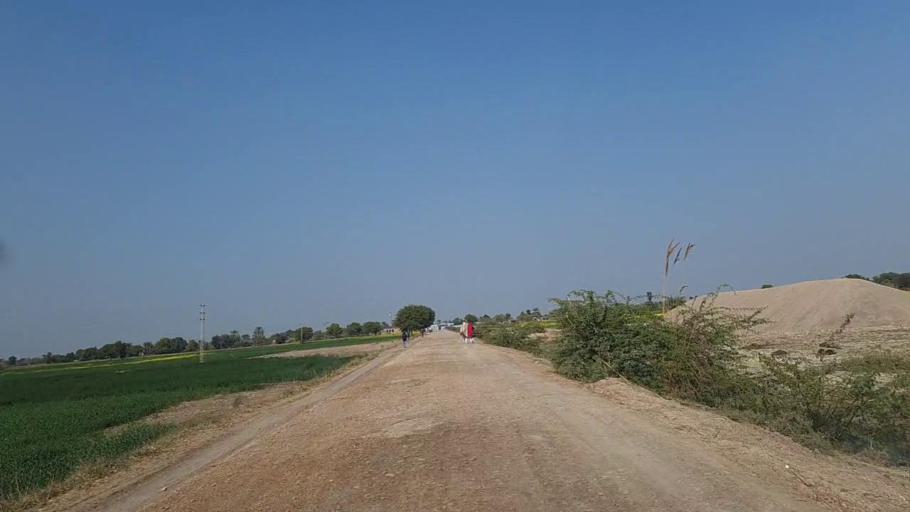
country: PK
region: Sindh
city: Jam Sahib
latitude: 26.2710
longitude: 68.5288
